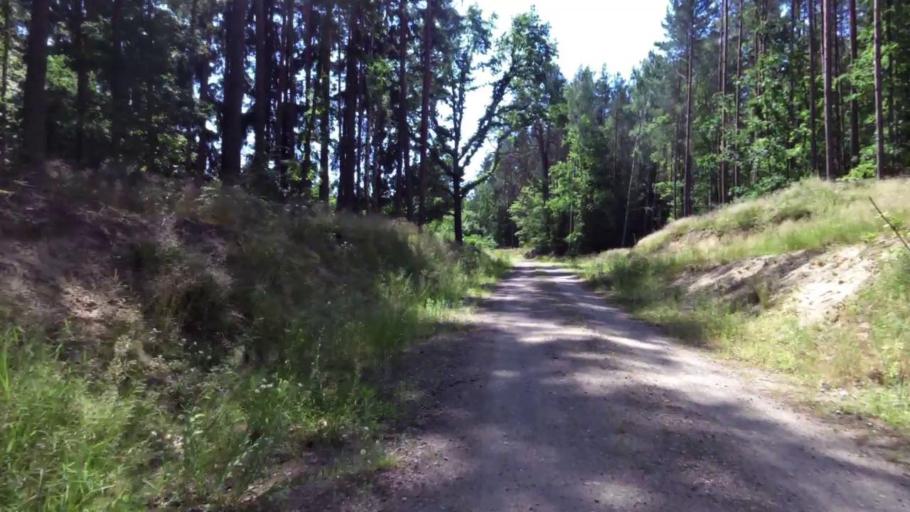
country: PL
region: West Pomeranian Voivodeship
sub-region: Powiat swidwinski
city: Polczyn-Zdroj
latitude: 53.7966
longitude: 16.1145
